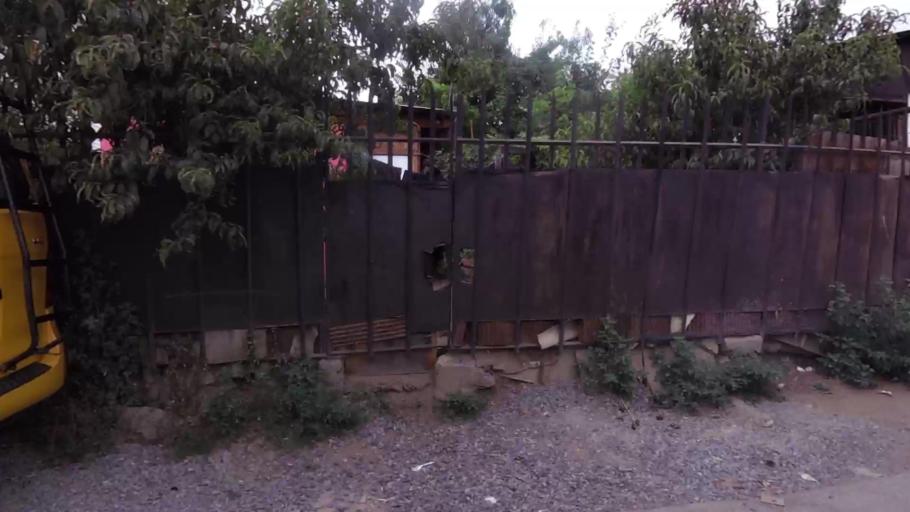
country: CL
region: O'Higgins
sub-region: Provincia de Cachapoal
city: Graneros
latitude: -34.0735
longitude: -70.7224
